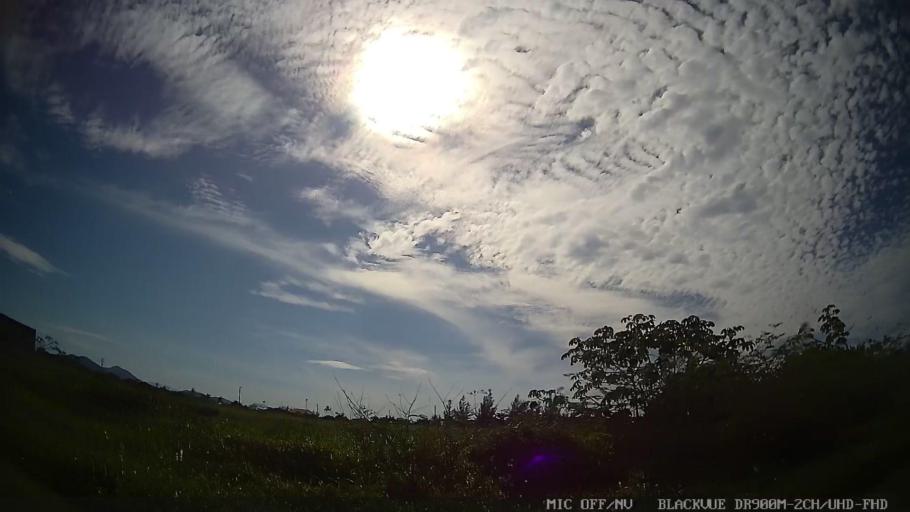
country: BR
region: Sao Paulo
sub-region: Iguape
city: Iguape
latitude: -24.7704
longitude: -47.5905
